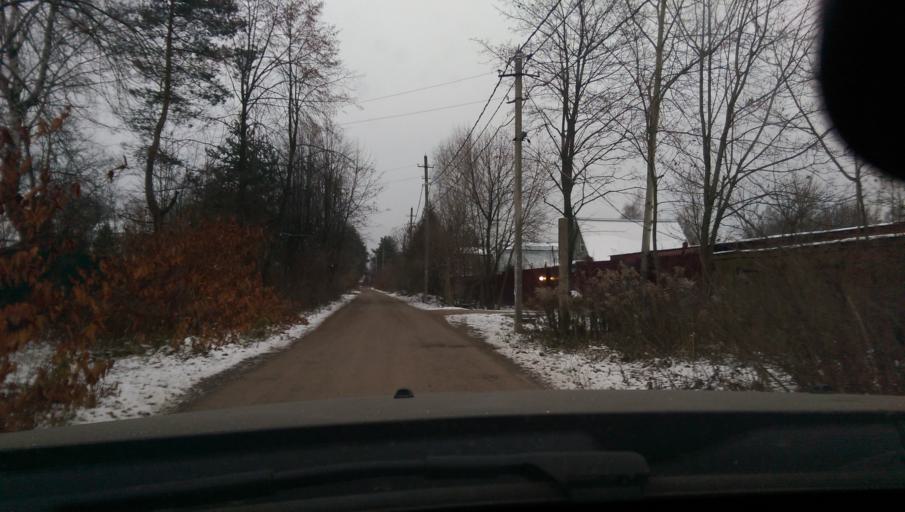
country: RU
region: Moskovskaya
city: Imeni Vorovskogo
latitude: 55.7314
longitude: 38.2850
